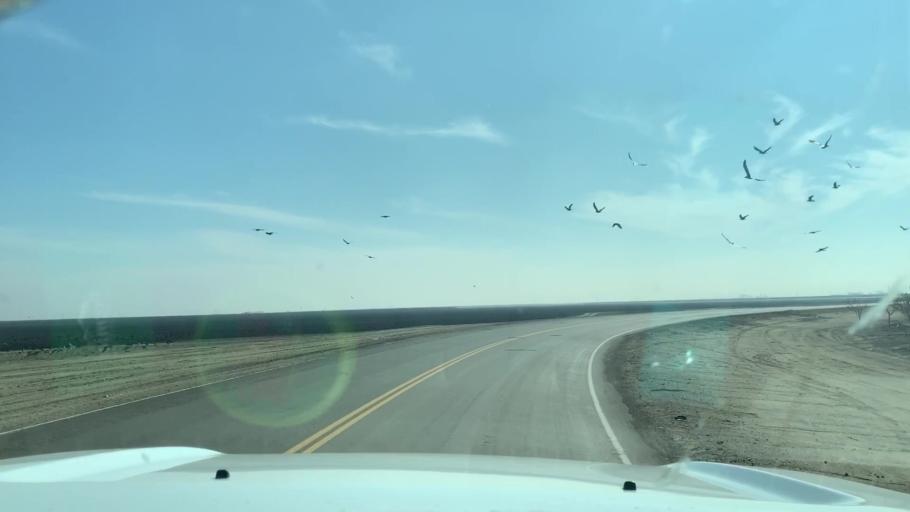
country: US
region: California
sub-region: Kern County
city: Buttonwillow
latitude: 35.4532
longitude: -119.5620
